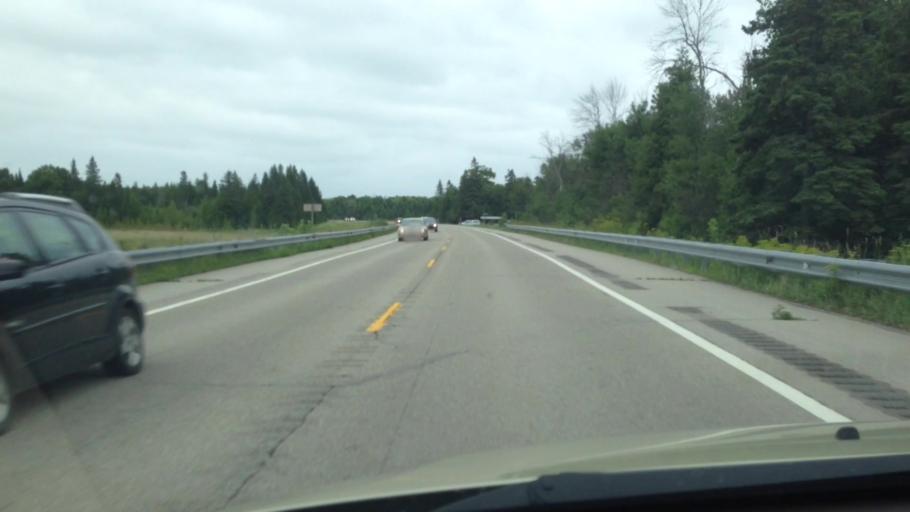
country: US
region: Michigan
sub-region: Mackinac County
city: Saint Ignace
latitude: 45.9163
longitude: -84.8742
